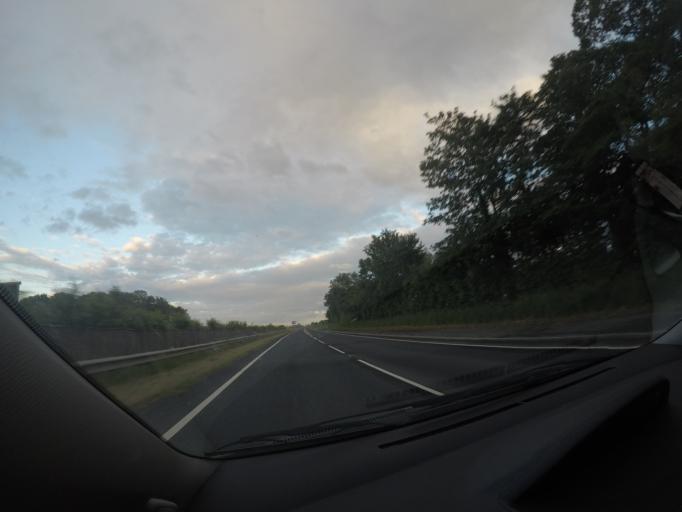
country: GB
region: England
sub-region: North Yorkshire
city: Bedale
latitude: 54.2922
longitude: -1.5512
